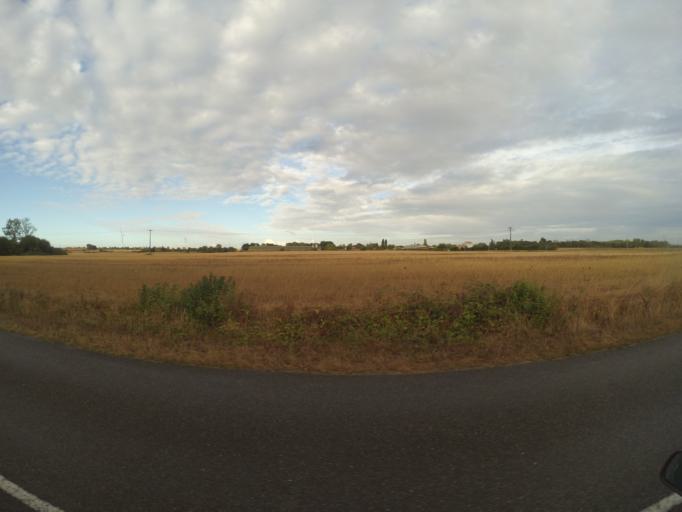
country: FR
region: Pays de la Loire
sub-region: Departement de la Loire-Atlantique
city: La Planche
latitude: 47.0106
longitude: -1.4559
